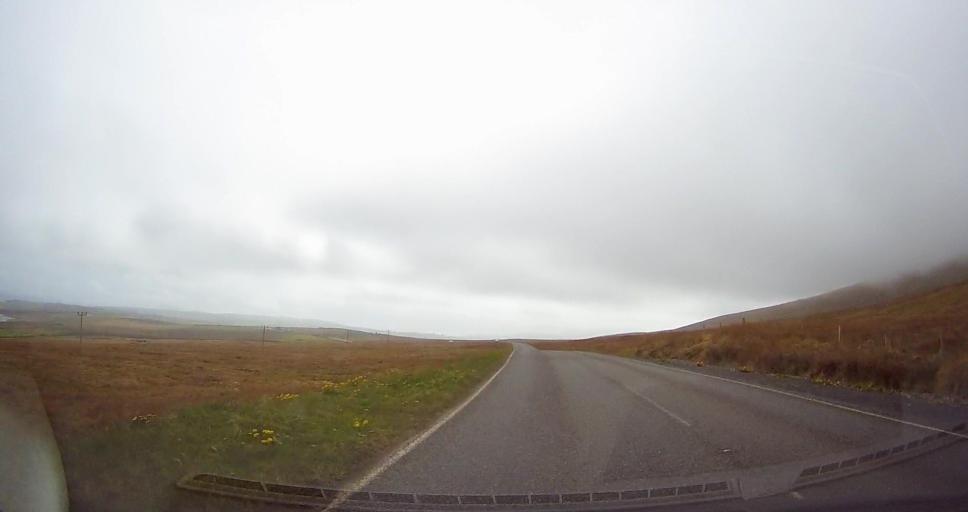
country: GB
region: Scotland
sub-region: Shetland Islands
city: Sandwick
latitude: 59.9537
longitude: -1.2906
